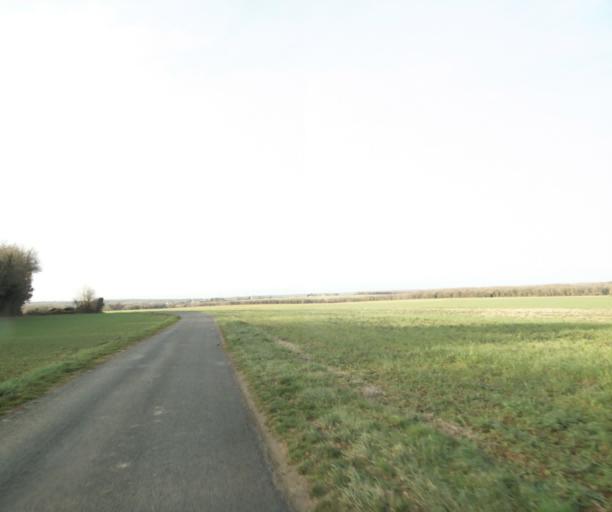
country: FR
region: Poitou-Charentes
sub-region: Departement de la Charente-Maritime
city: Fontcouverte
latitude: 45.8182
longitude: -0.5791
